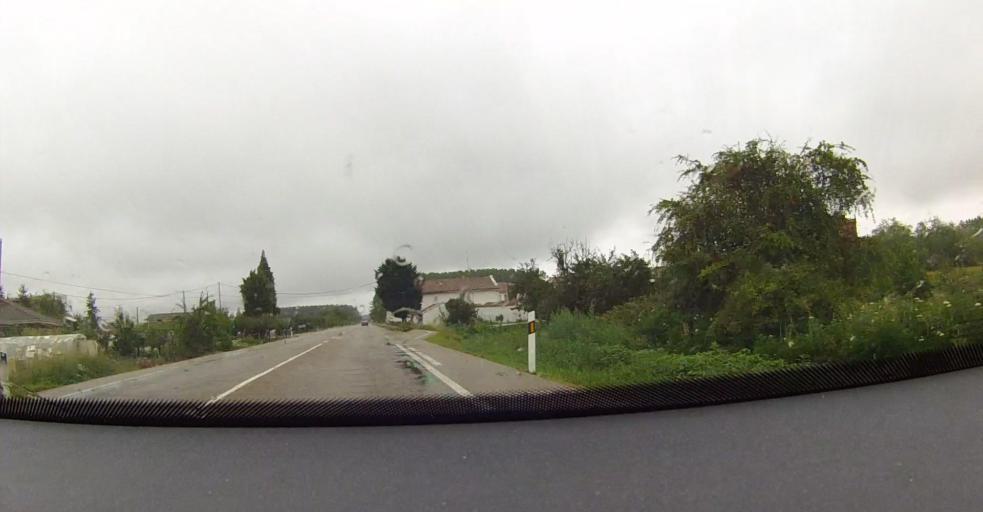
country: ES
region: Castille and Leon
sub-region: Provincia de Palencia
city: Saldana
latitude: 42.4982
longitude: -4.7290
